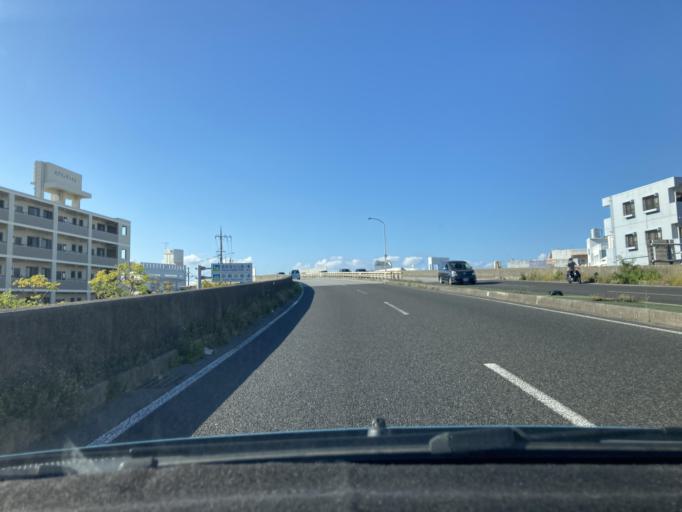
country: JP
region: Okinawa
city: Ginowan
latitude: 26.2526
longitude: 127.7403
